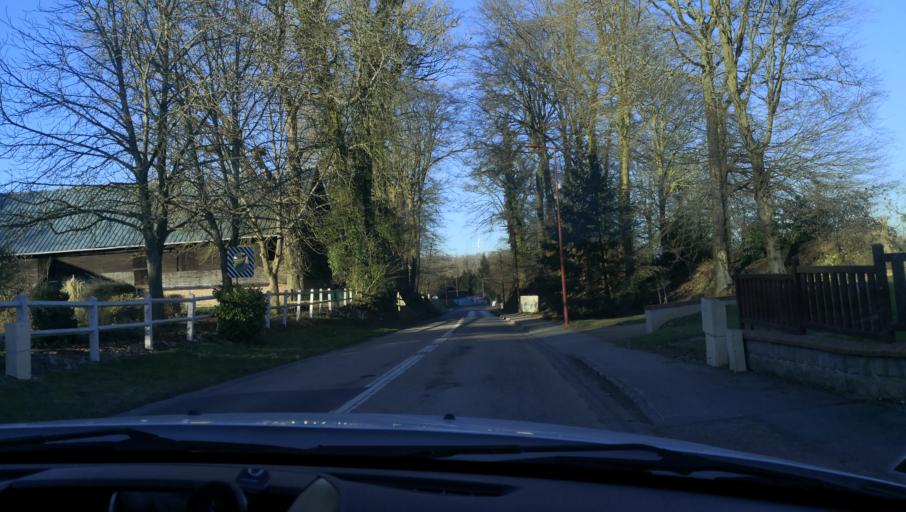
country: FR
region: Haute-Normandie
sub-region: Departement de la Seine-Maritime
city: Totes
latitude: 49.6652
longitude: 1.0253
